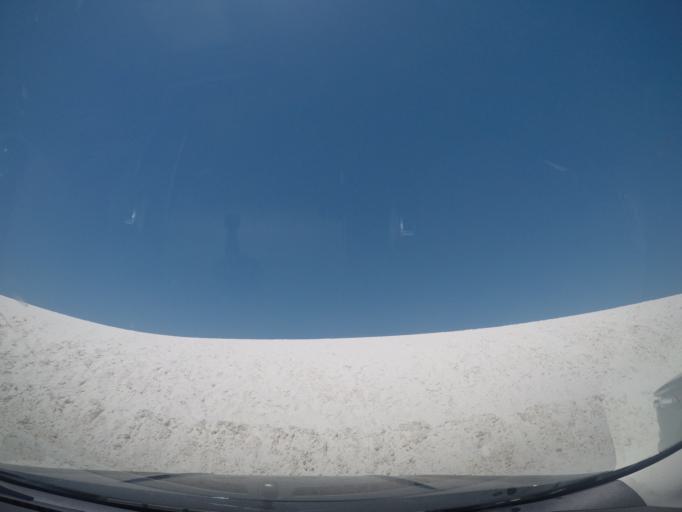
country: US
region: New Mexico
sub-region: Otero County
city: Holloman Air Force Base
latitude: 32.8225
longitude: -106.2724
